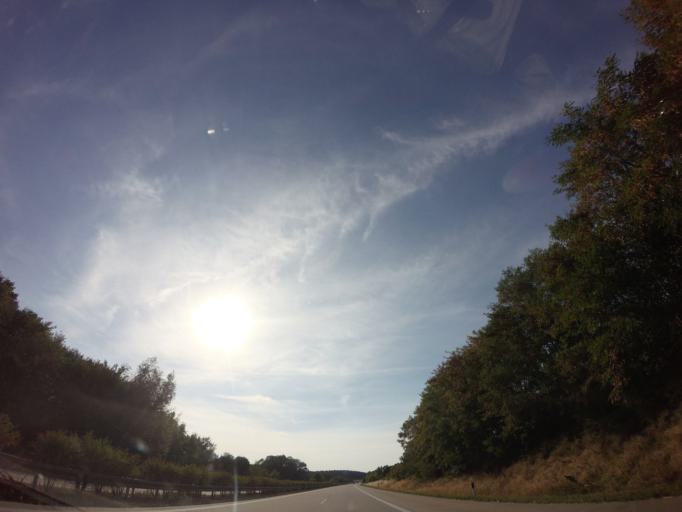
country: DE
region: Mecklenburg-Vorpommern
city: Siggelkow
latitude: 53.2980
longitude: 11.9507
